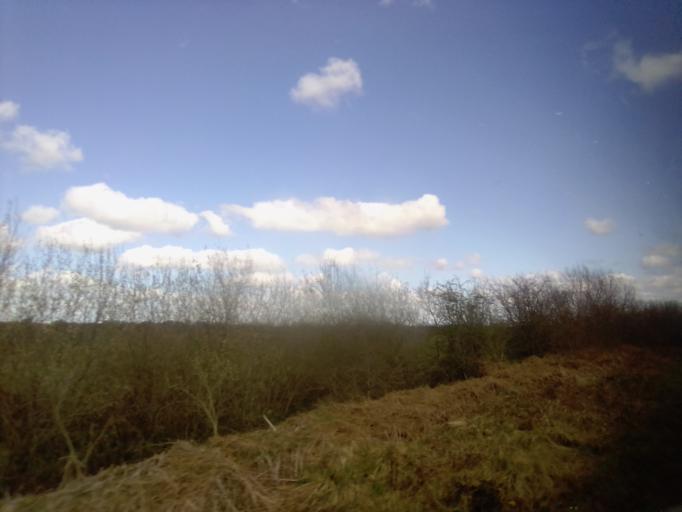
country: IE
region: Munster
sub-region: County Cork
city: Millstreet
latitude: 52.0840
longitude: -9.2014
